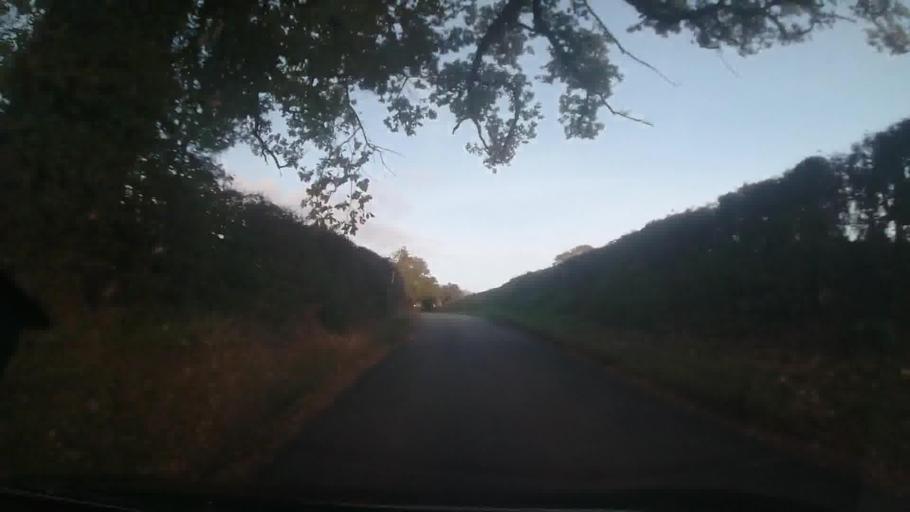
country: GB
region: England
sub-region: Shropshire
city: Clive
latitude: 52.8113
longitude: -2.7340
